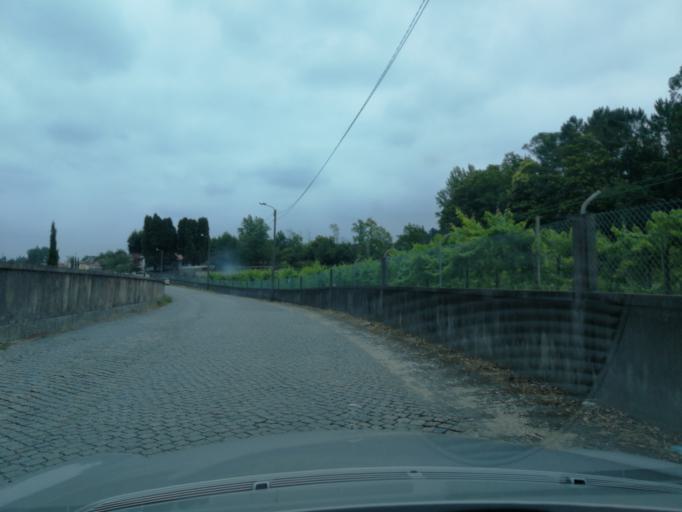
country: PT
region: Braga
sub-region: Vila Verde
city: Prado
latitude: 41.6008
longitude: -8.4411
